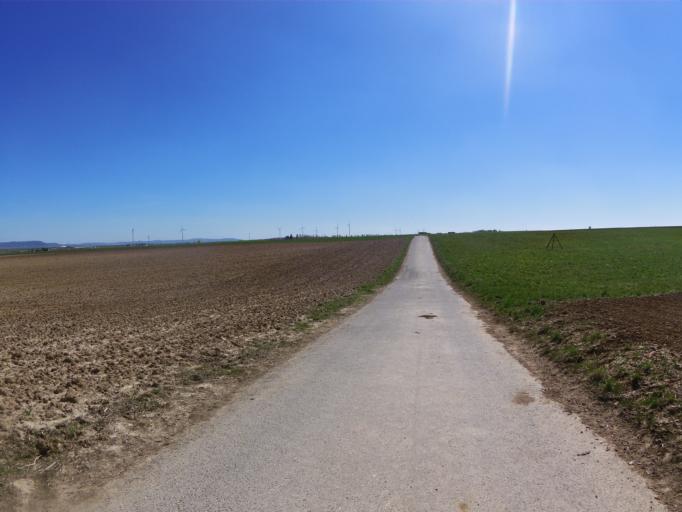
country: DE
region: Bavaria
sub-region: Regierungsbezirk Unterfranken
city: Biebelried
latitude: 49.8083
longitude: 10.0878
